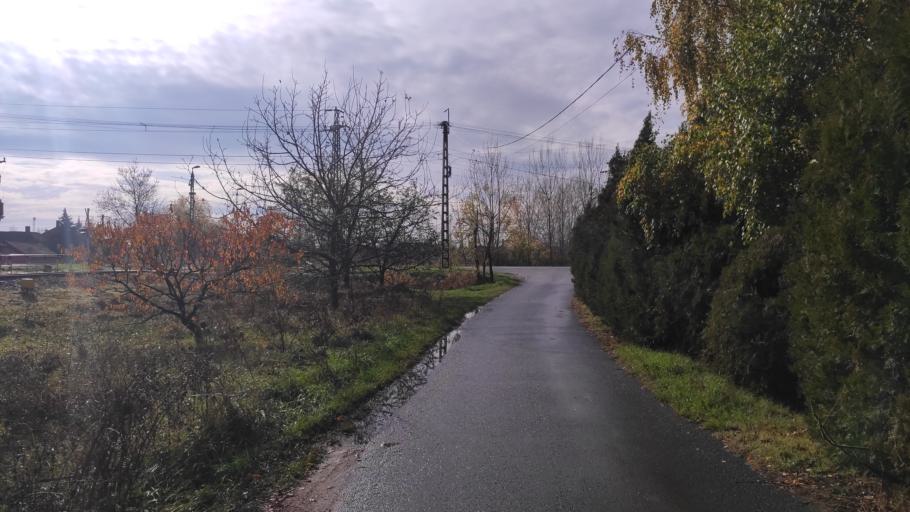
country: HU
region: Bekes
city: Mezobereny
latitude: 46.7627
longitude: 21.0376
